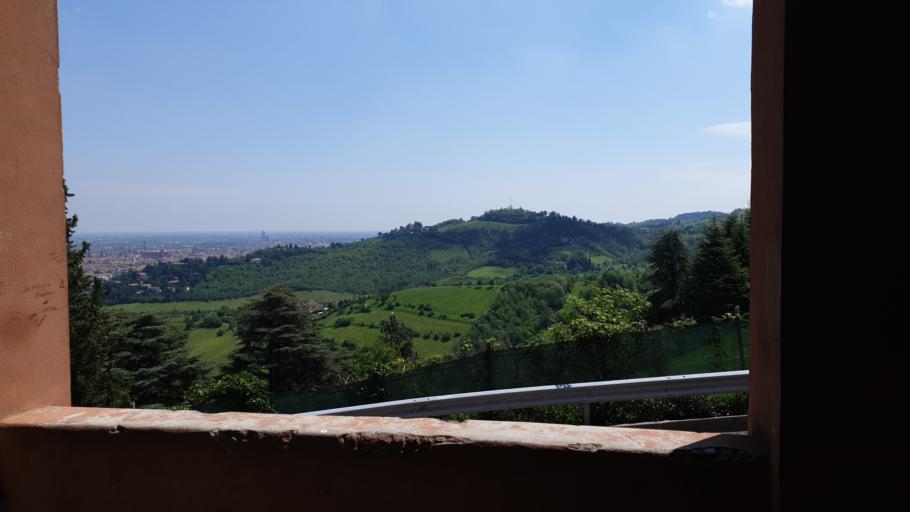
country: IT
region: Emilia-Romagna
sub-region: Provincia di Bologna
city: Casalecchio di Reno
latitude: 44.4825
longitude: 11.3027
